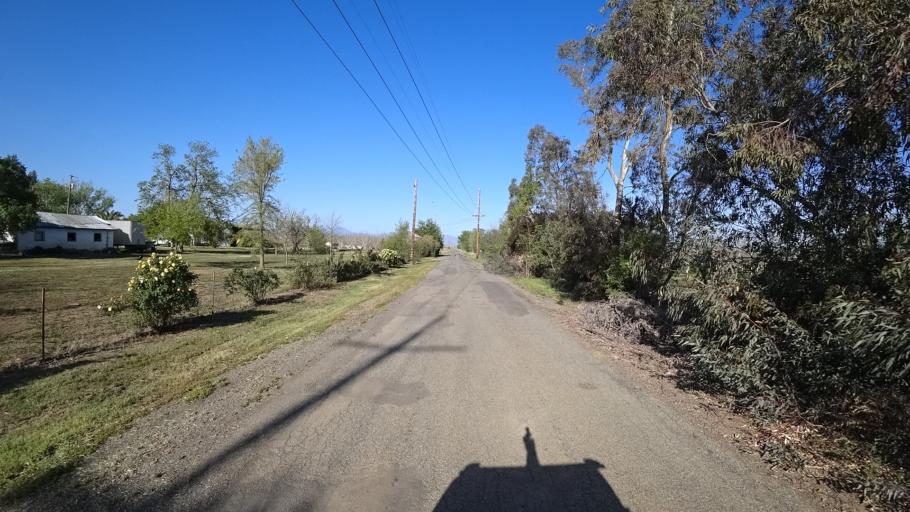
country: US
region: California
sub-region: Glenn County
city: Willows
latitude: 39.5534
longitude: -122.2313
